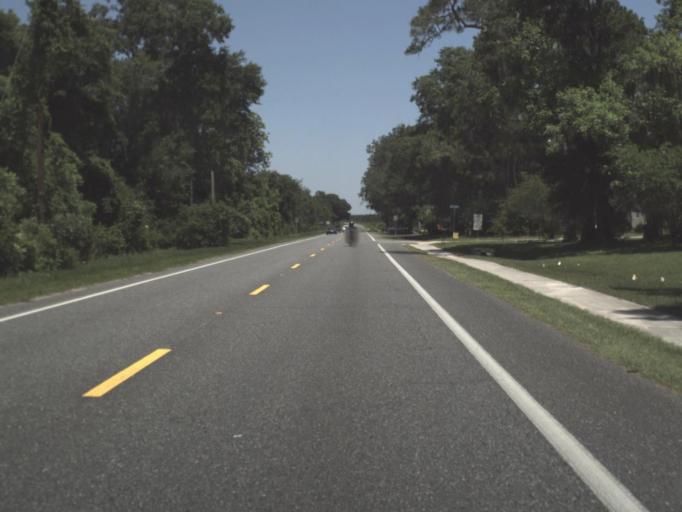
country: US
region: Florida
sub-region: Columbia County
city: Watertown
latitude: 30.2048
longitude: -82.4241
